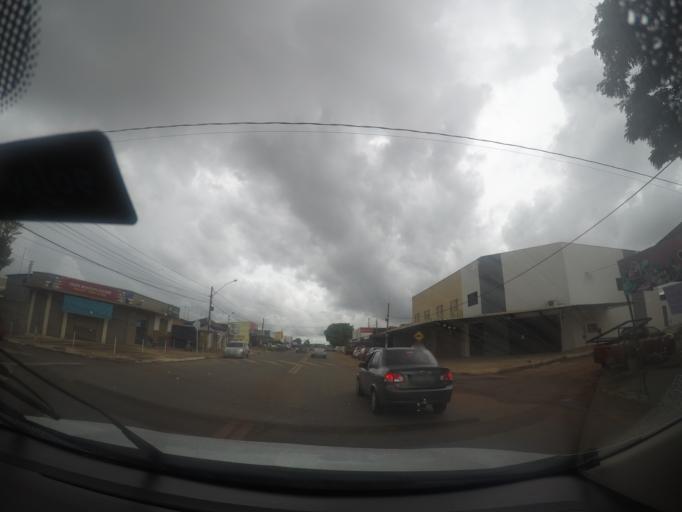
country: BR
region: Goias
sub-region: Trindade
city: Trindade
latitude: -16.6366
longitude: -49.3903
